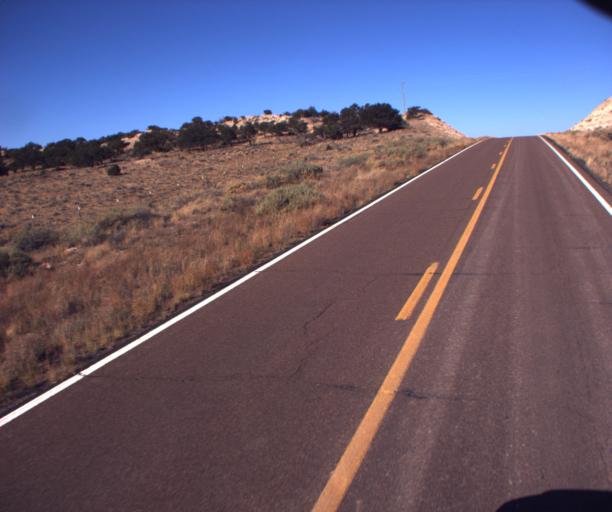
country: US
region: Arizona
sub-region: Navajo County
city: First Mesa
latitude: 35.7625
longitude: -109.9739
